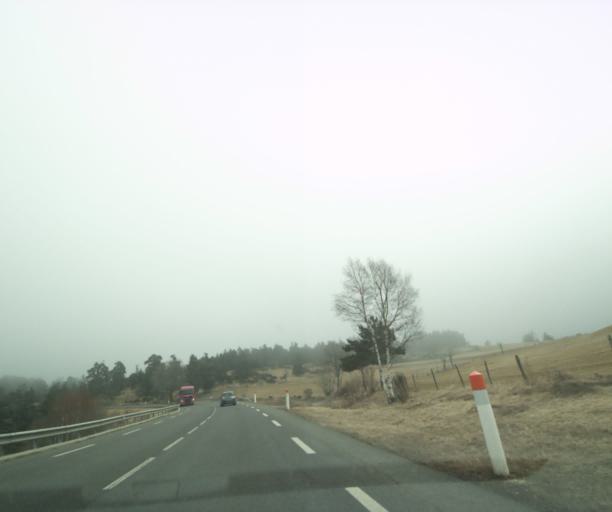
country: FR
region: Languedoc-Roussillon
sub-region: Departement de la Lozere
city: Langogne
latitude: 44.6752
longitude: 3.7685
